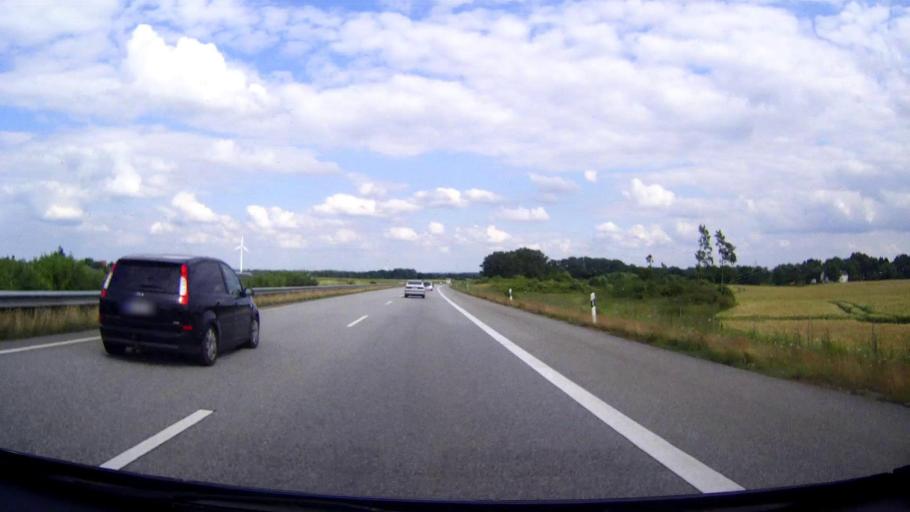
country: DE
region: Schleswig-Holstein
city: Monkhagen
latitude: 53.9152
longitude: 10.5315
